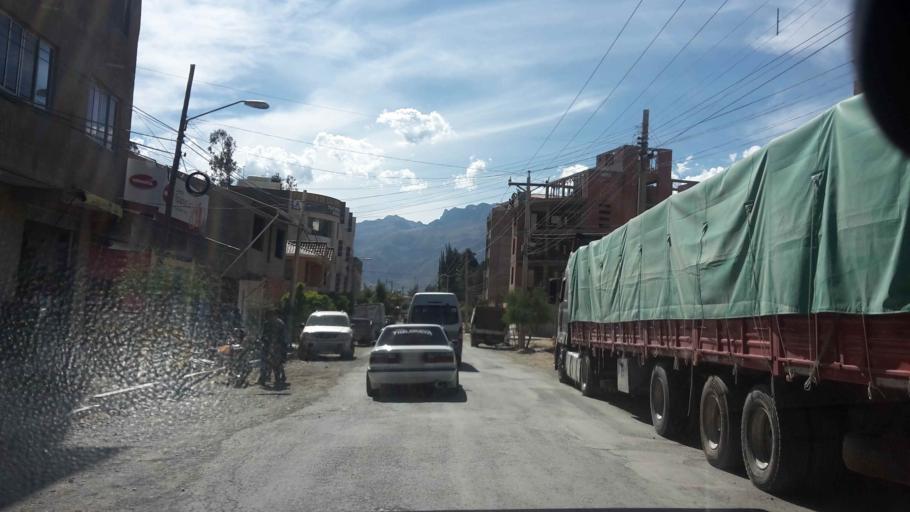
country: BO
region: Cochabamba
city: Cochabamba
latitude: -17.3368
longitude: -66.2222
